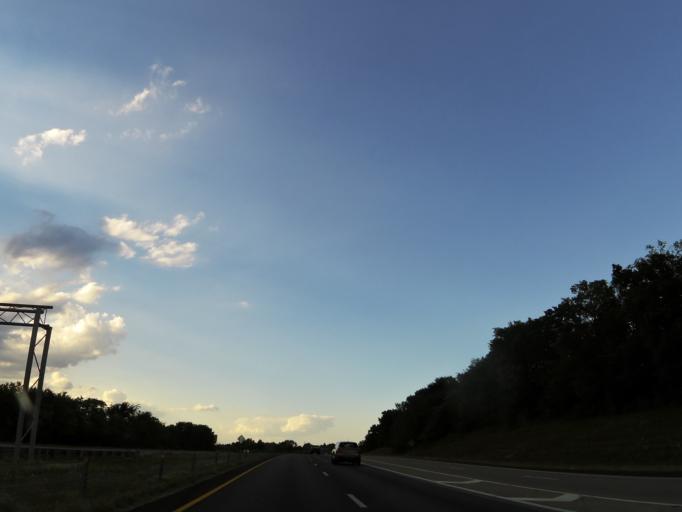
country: US
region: Tennessee
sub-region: Maury County
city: Spring Hill
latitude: 35.7471
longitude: -86.8713
